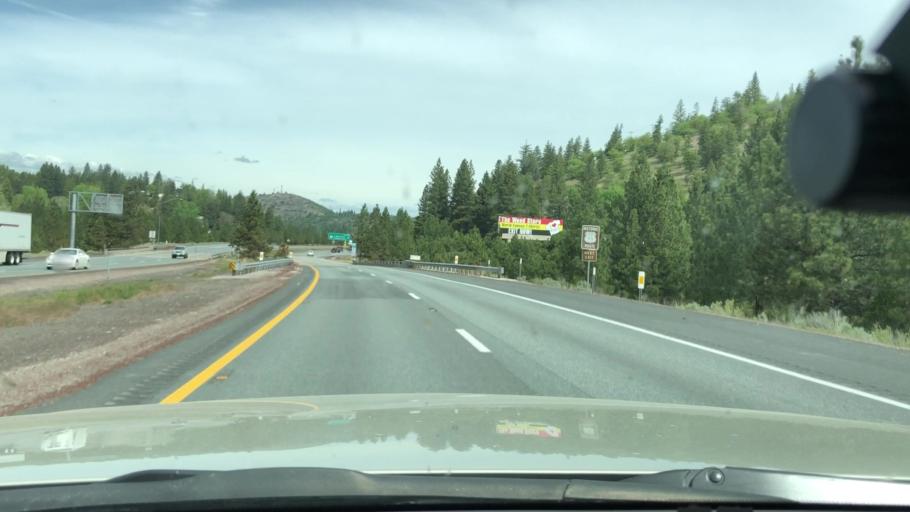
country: US
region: California
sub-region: Siskiyou County
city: Weed
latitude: 41.4126
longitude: -122.3804
